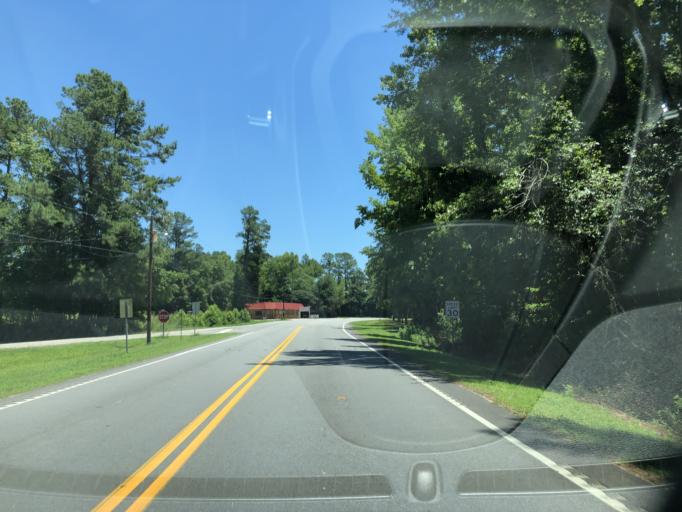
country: US
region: South Carolina
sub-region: Orangeburg County
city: Branchville
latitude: 33.2508
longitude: -80.8272
